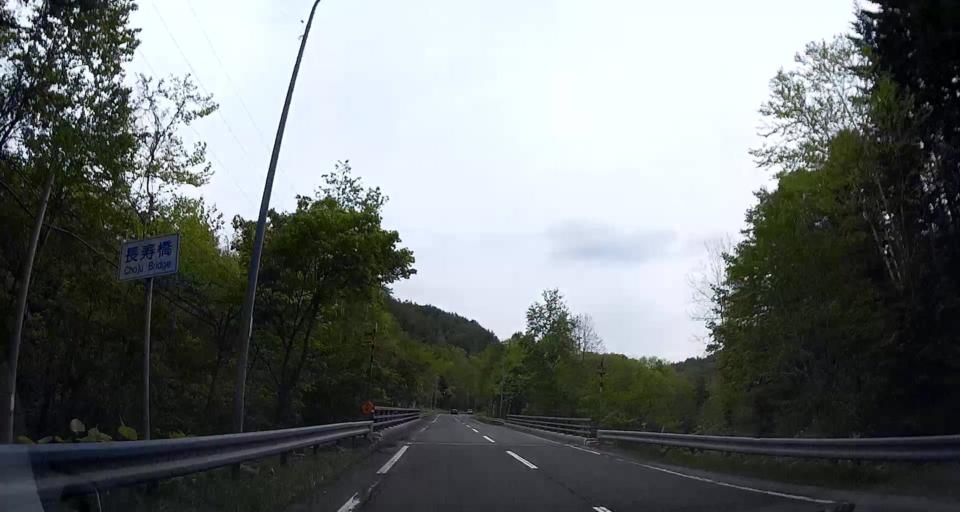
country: JP
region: Hokkaido
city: Shiraoi
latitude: 42.6862
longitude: 141.1026
